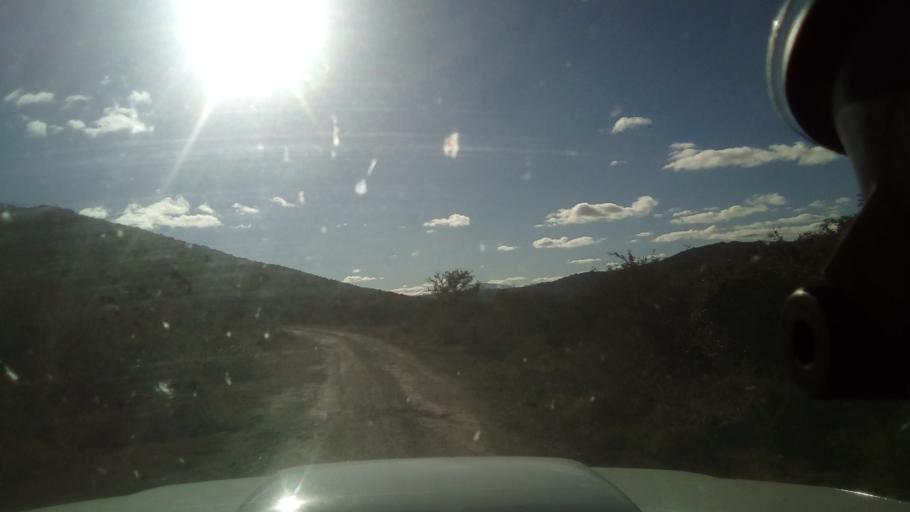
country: ZA
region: Eastern Cape
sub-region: Buffalo City Metropolitan Municipality
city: Bhisho
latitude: -32.7419
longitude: 27.3500
